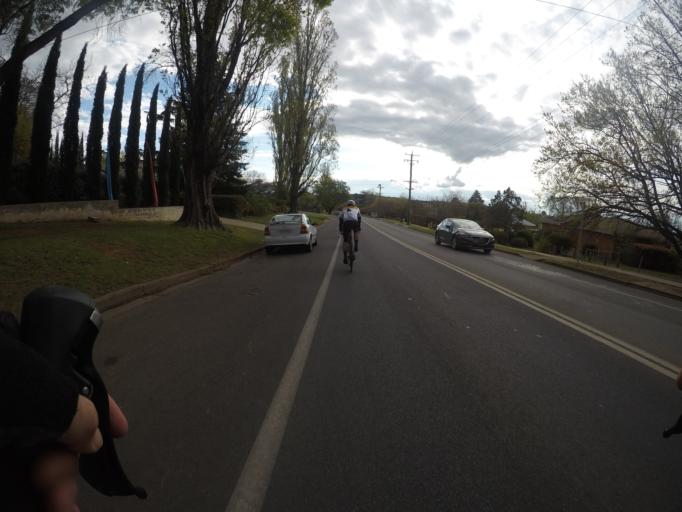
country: AU
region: New South Wales
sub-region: Orange Municipality
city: Orange
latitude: -33.2808
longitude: 149.0762
